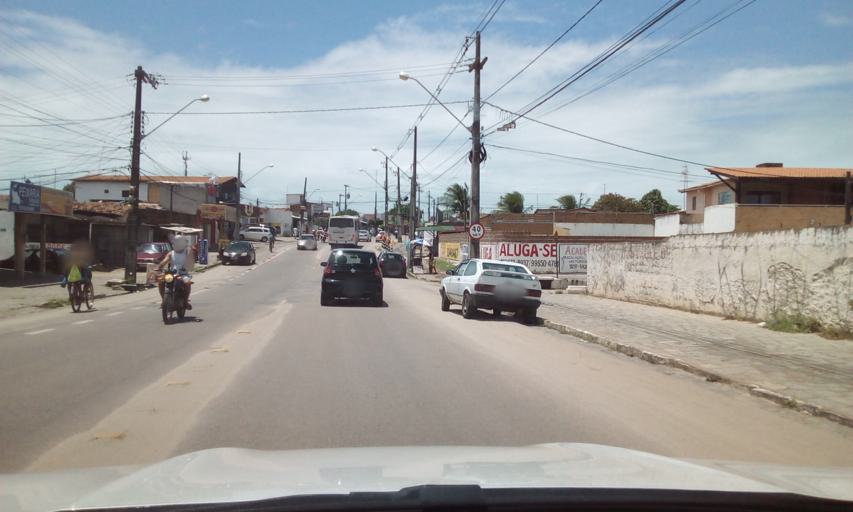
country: BR
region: Paraiba
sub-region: Conde
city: Conde
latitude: -7.2047
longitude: -34.8494
